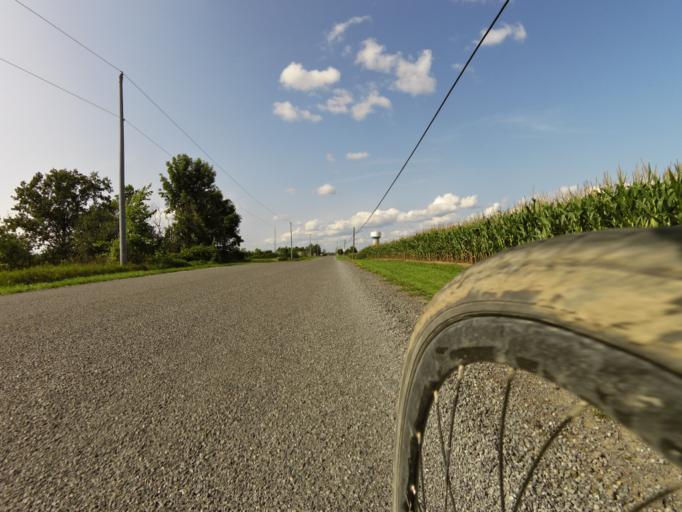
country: CA
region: Ontario
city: Kingston
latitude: 44.3993
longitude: -76.5962
